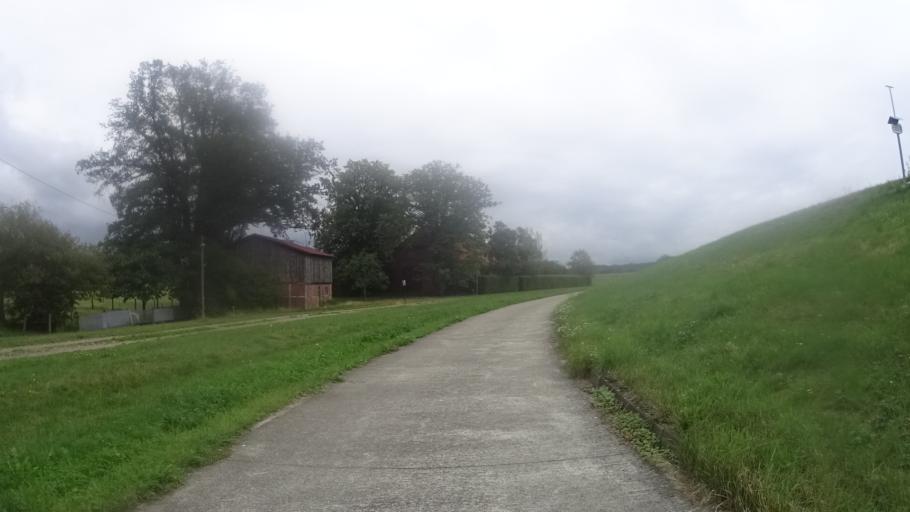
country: DE
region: Lower Saxony
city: Tosterglope
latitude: 53.2701
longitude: 10.8286
